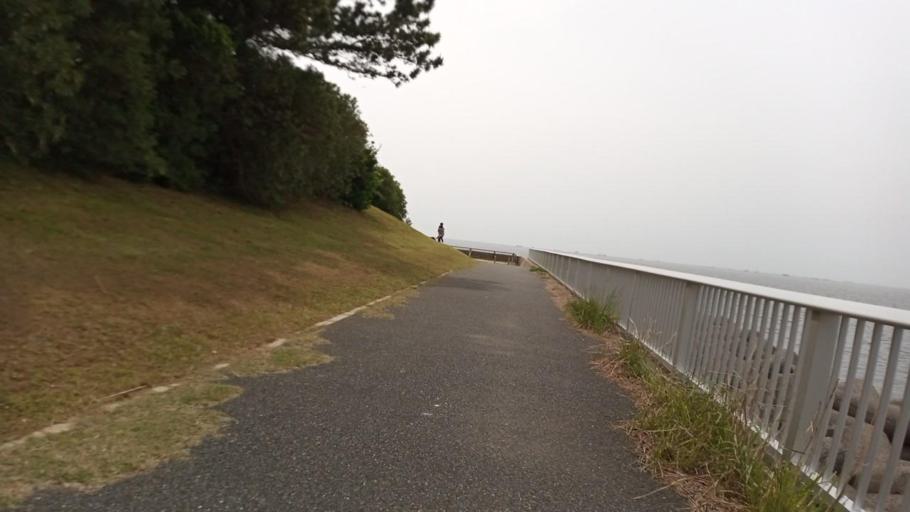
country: JP
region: Chiba
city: Funabashi
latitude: 35.6458
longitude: 140.0292
